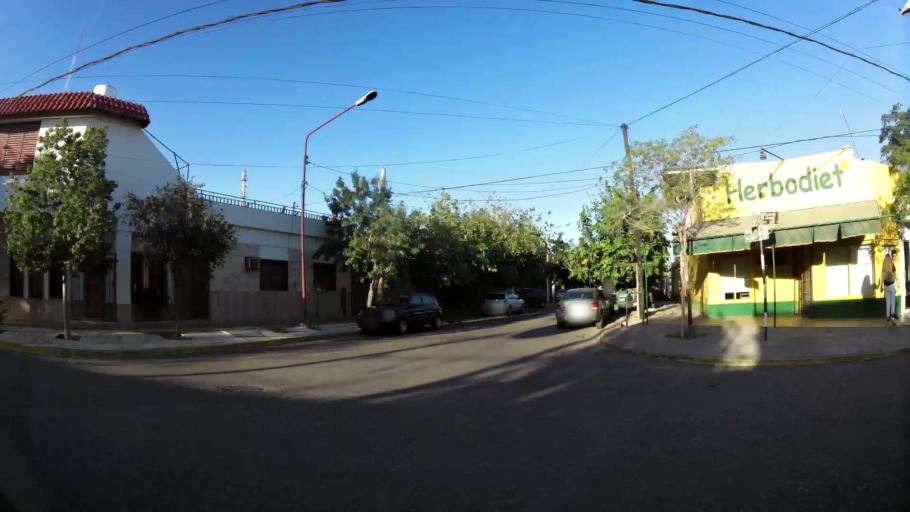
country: AR
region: San Juan
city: San Juan
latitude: -31.5481
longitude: -68.5288
